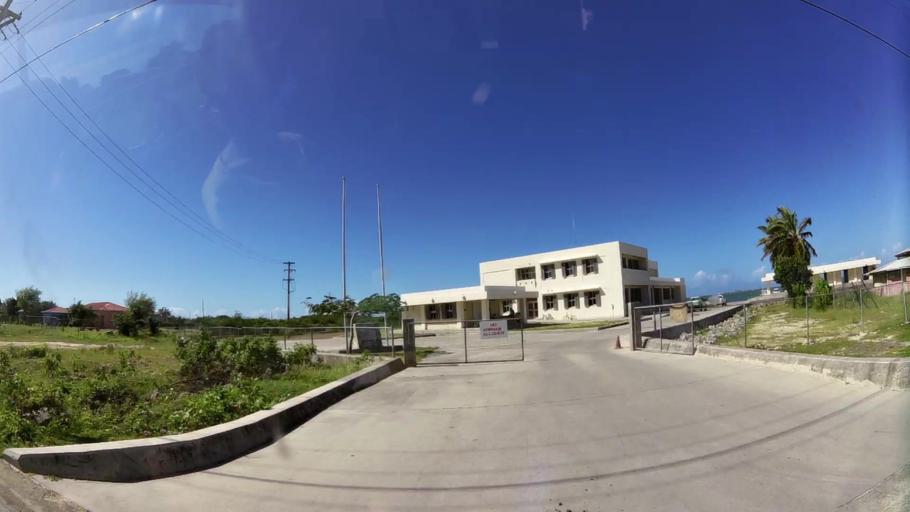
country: AG
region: Barbuda
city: Codrington
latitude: 17.6410
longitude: -61.8280
